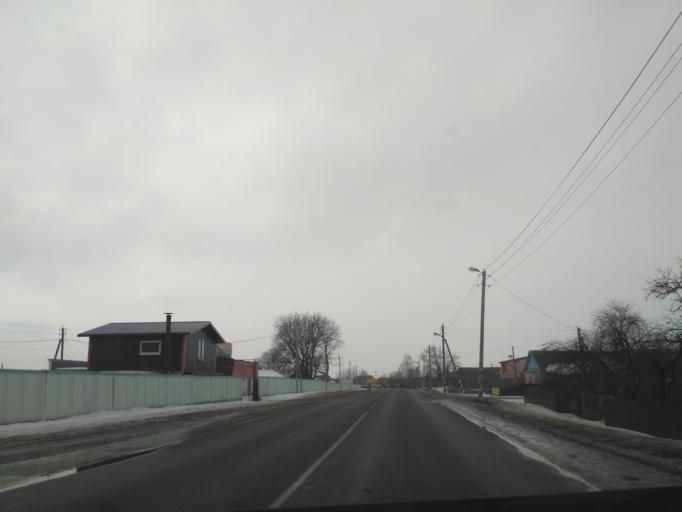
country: BY
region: Minsk
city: Horad Smalyavichy
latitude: 54.0257
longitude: 28.0684
